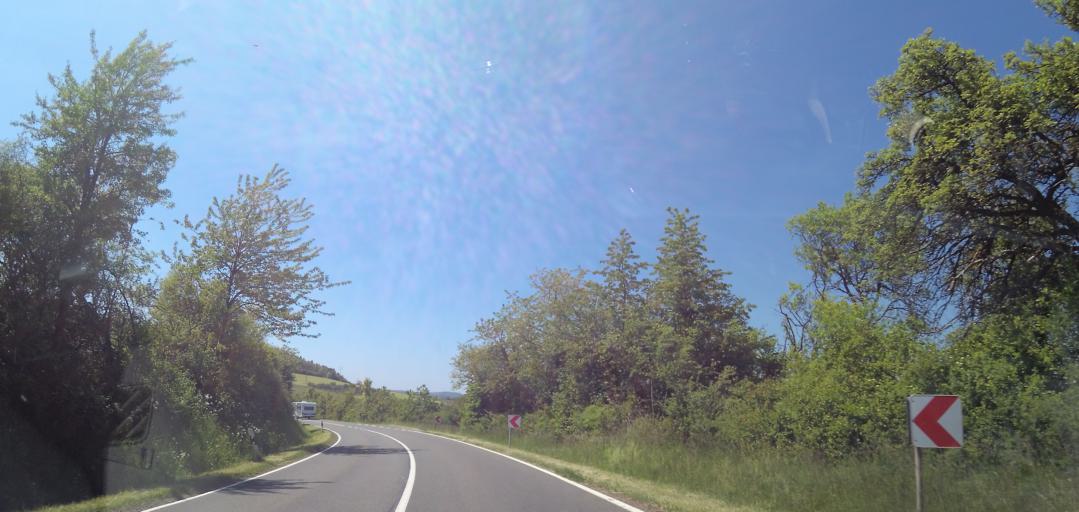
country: DE
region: Saarland
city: Britten
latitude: 49.4651
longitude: 6.7021
